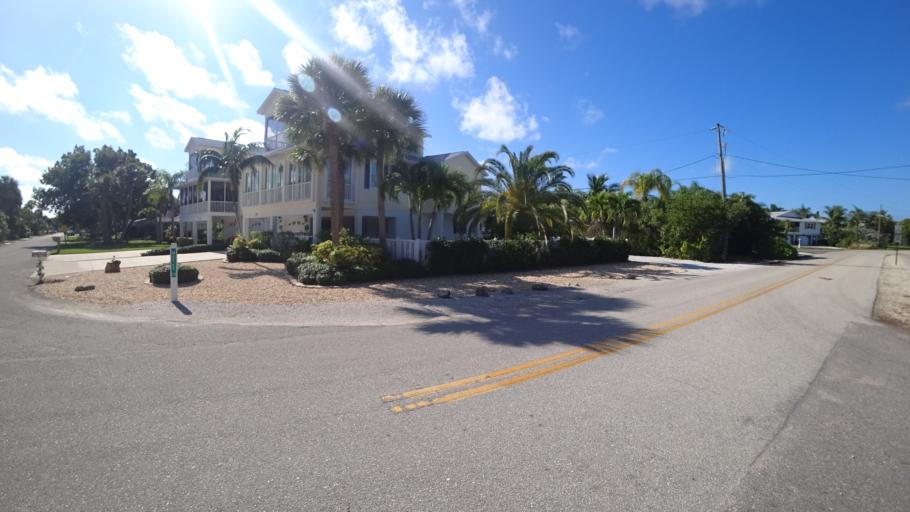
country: US
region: Florida
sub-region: Manatee County
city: Anna Maria
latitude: 27.5229
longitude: -82.7256
